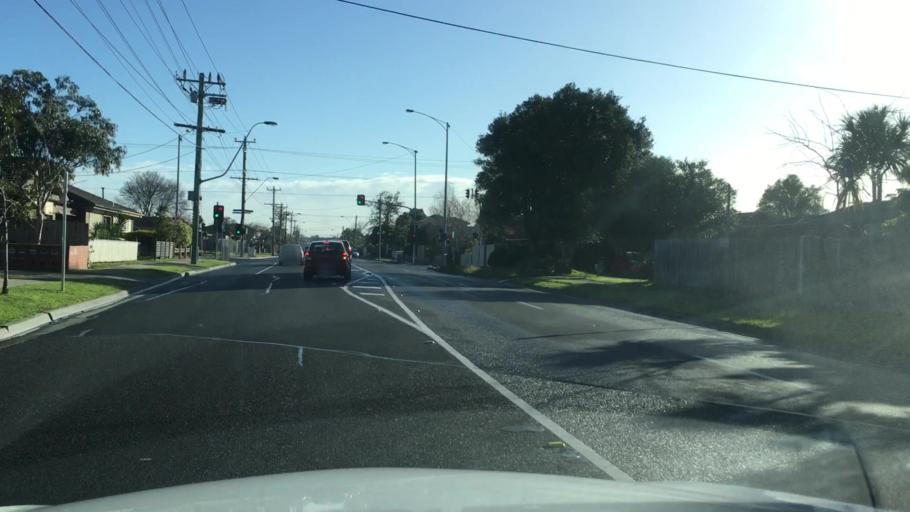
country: AU
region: Victoria
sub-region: Greater Dandenong
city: Noble Park
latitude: -37.9686
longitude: 145.1677
